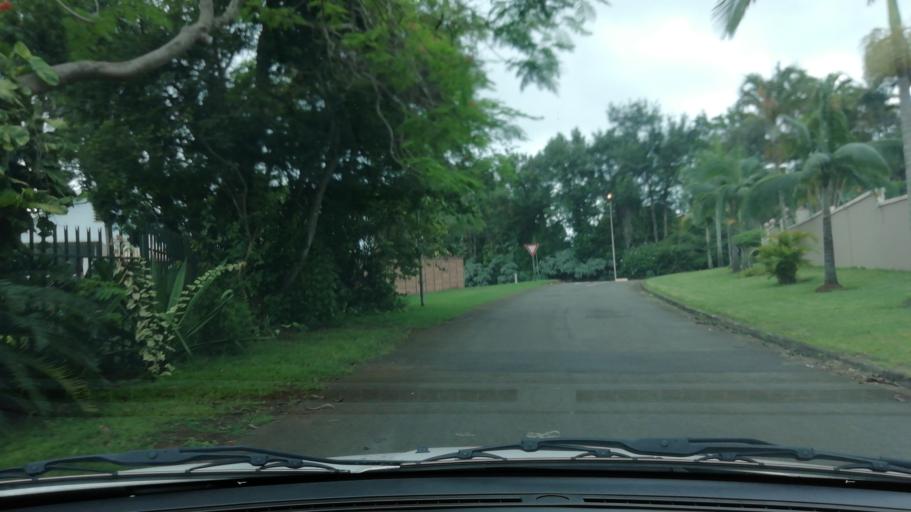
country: ZA
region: KwaZulu-Natal
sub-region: uThungulu District Municipality
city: Empangeni
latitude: -28.7615
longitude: 31.8943
